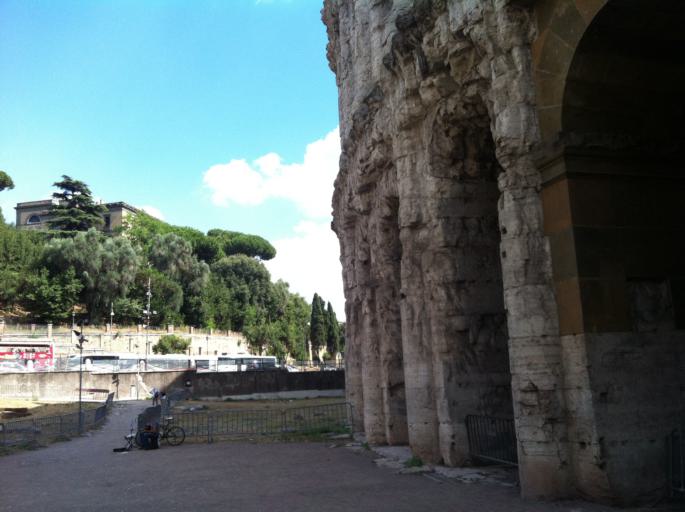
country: VA
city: Vatican City
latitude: 41.8923
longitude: 12.4795
